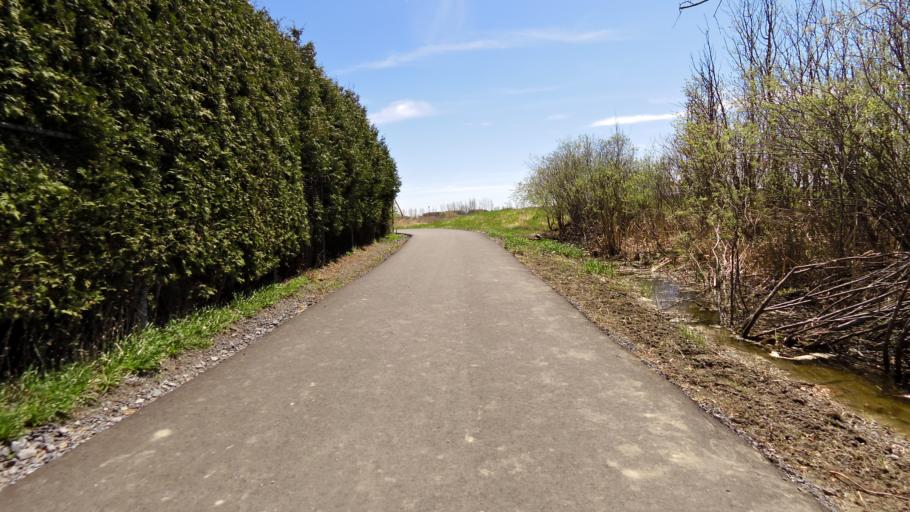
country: CA
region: Ontario
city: Clarence-Rockland
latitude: 45.4591
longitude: -75.4826
